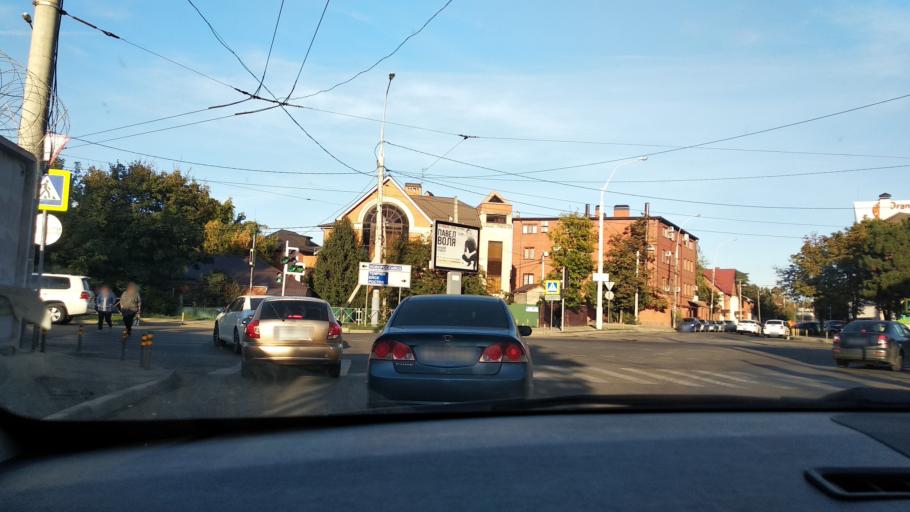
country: RU
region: Adygeya
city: Yablonovskiy
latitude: 45.0139
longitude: 38.9586
